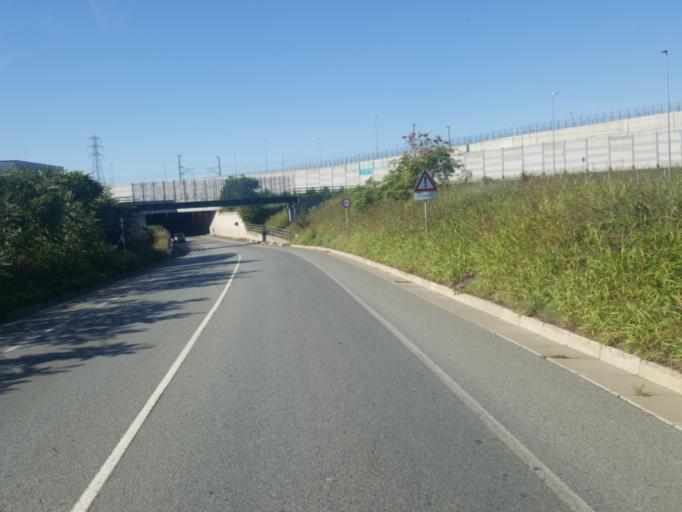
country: IT
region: Lombardy
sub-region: Citta metropolitana di Milano
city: Arluno
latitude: 45.4981
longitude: 8.9279
